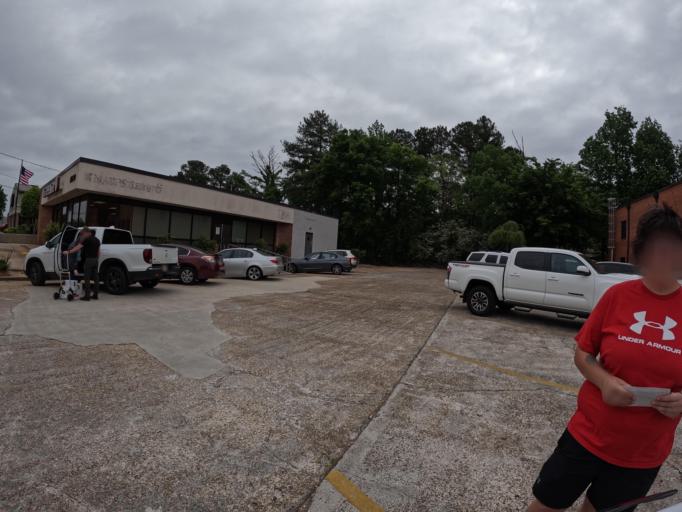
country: US
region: Mississippi
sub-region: Lee County
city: Tupelo
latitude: 34.2785
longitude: -88.7151
